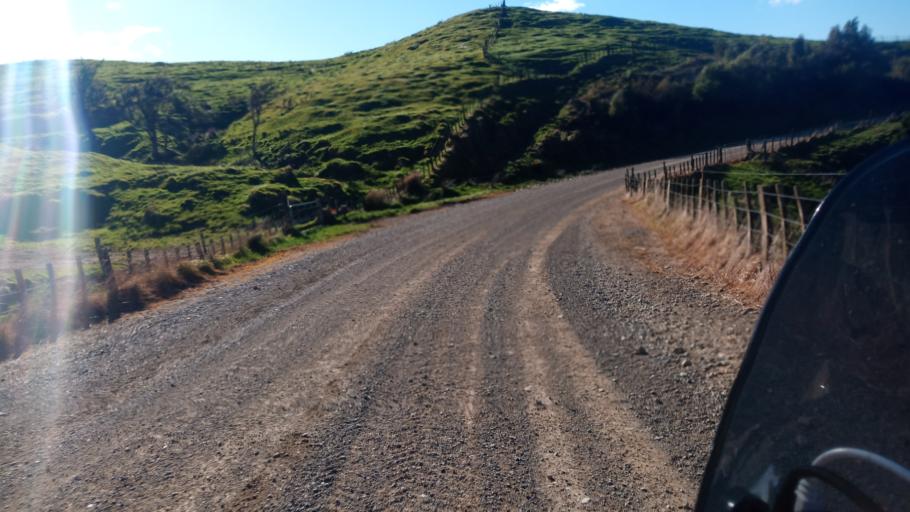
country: NZ
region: Hawke's Bay
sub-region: Wairoa District
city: Wairoa
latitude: -38.7395
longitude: 177.2870
